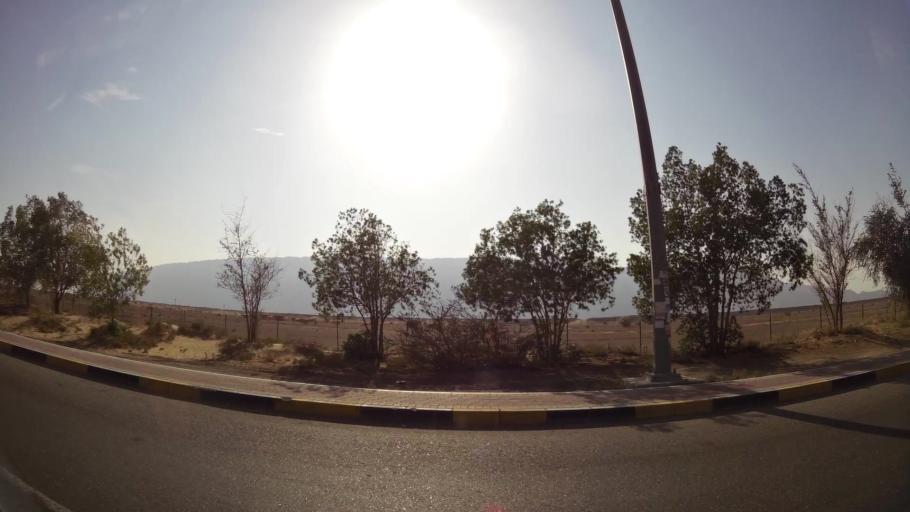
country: AE
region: Abu Dhabi
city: Al Ain
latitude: 24.0640
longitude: 55.8372
